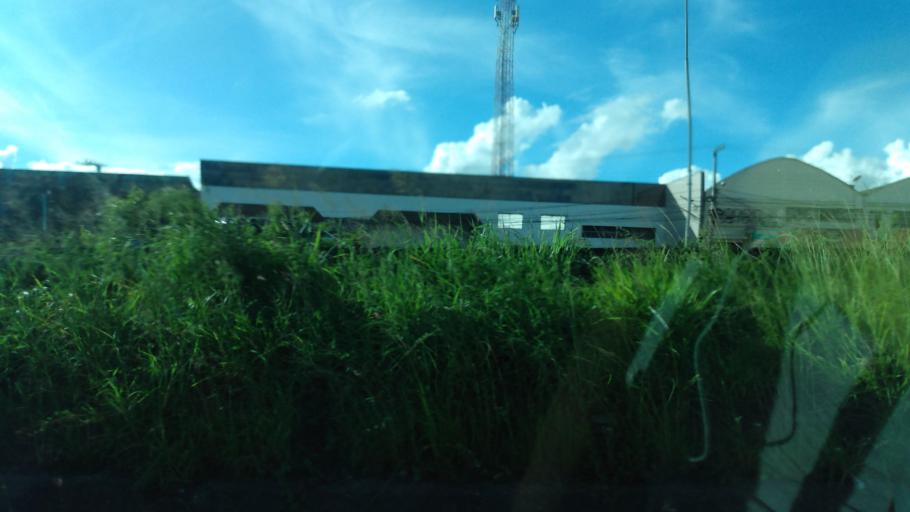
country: ET
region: Oromiya
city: Gore
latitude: 8.1968
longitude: 35.5757
